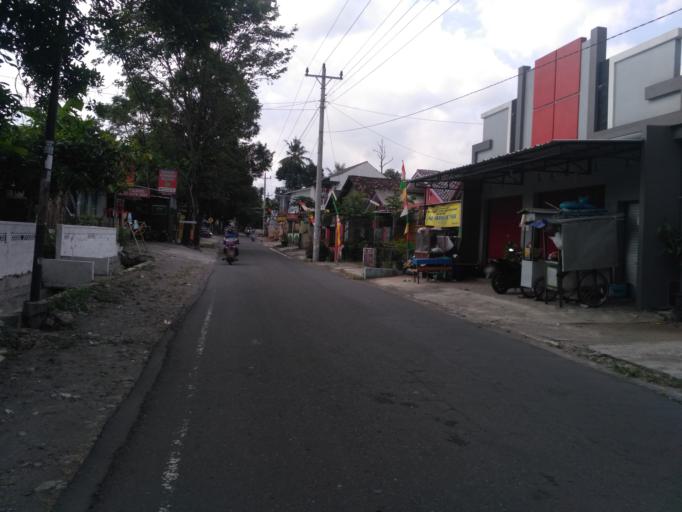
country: ID
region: Daerah Istimewa Yogyakarta
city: Sleman
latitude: -7.7249
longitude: 110.3573
